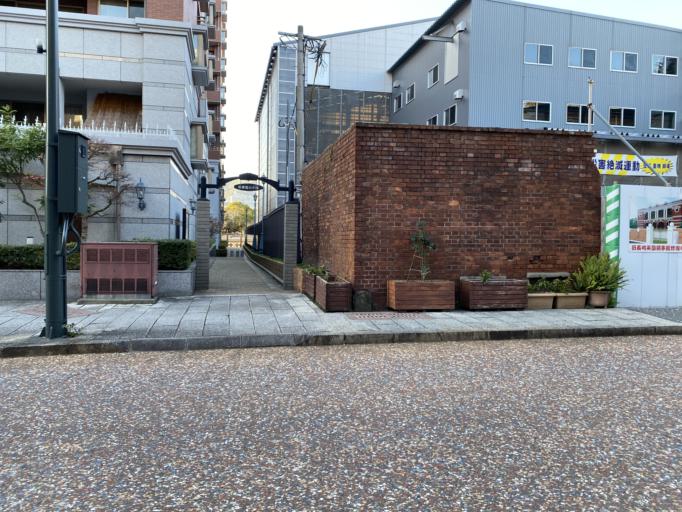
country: JP
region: Nagasaki
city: Nagasaki-shi
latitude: 32.7382
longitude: 129.8718
